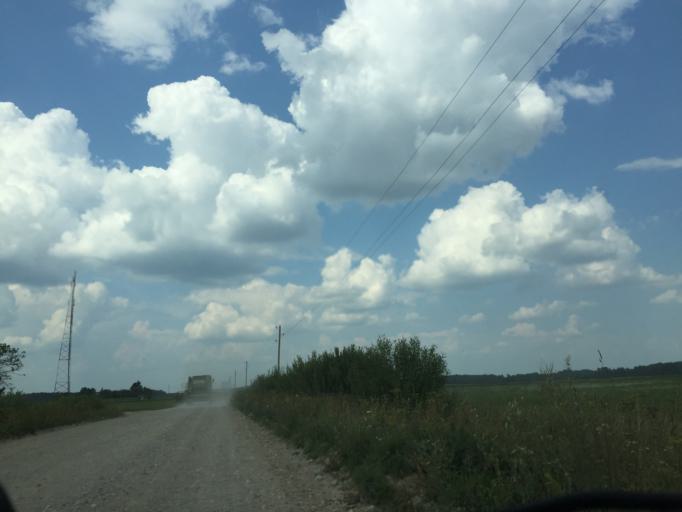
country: LT
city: Naujoji Akmene
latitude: 56.3507
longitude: 23.0592
